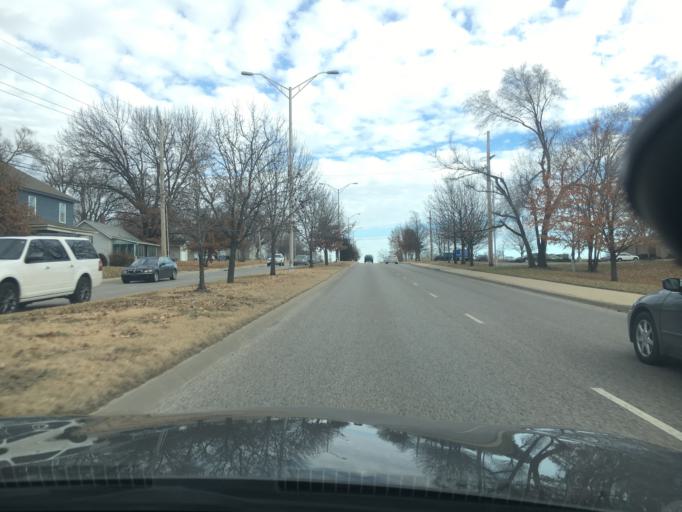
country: US
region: Kansas
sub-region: Johnson County
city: Leawood
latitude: 38.8545
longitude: -94.6632
